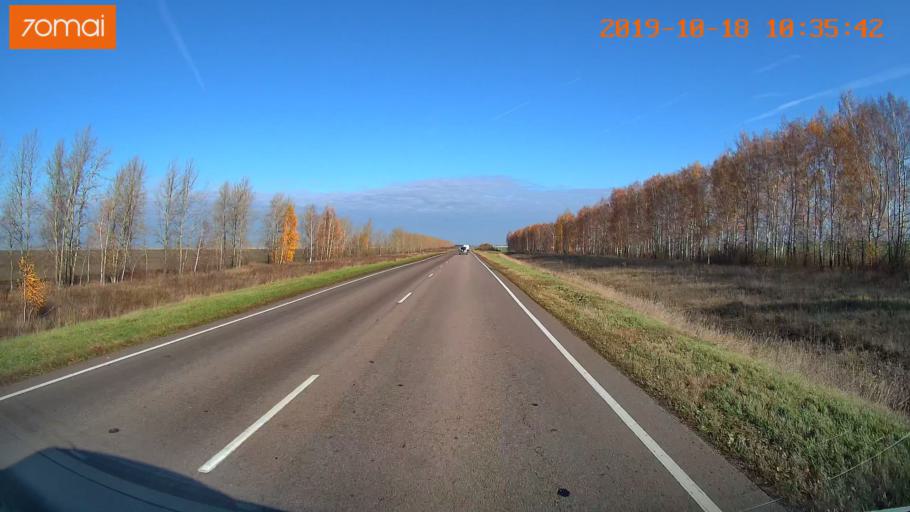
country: RU
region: Tula
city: Kurkino
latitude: 53.5372
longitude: 38.6209
